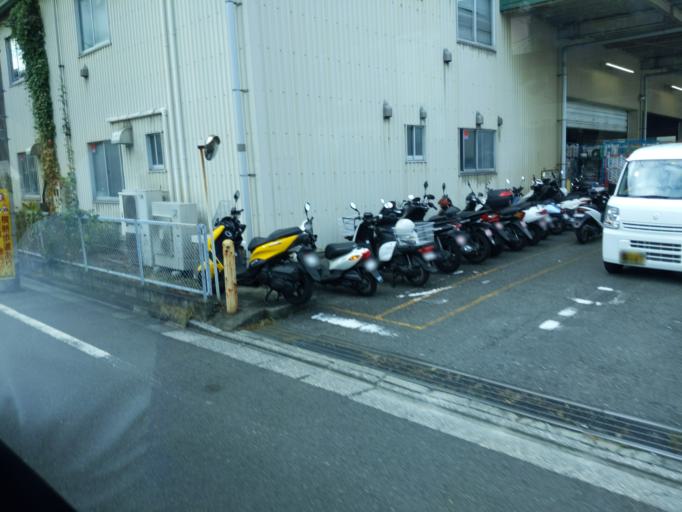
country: JP
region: Kanagawa
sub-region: Kawasaki-shi
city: Kawasaki
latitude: 35.5872
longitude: 139.6919
